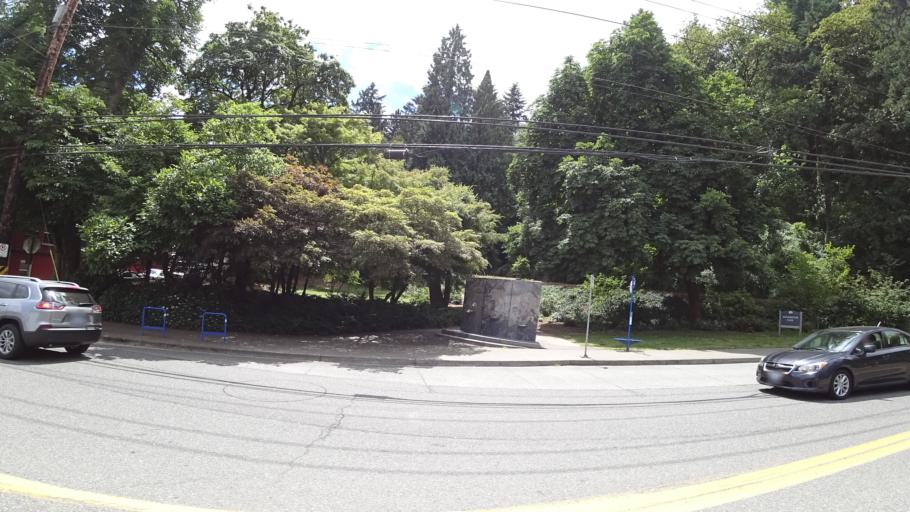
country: US
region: Oregon
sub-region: Multnomah County
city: Portland
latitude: 45.5239
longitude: -122.7008
